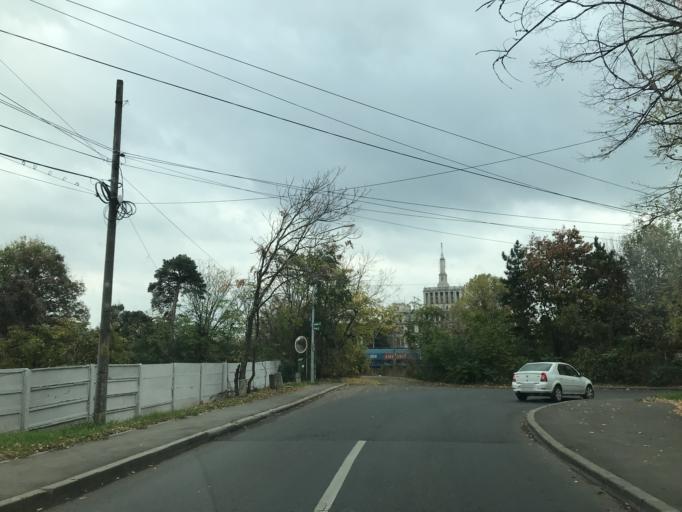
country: RO
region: Bucuresti
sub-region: Municipiul Bucuresti
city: Bucuresti
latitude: 44.4849
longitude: 26.0679
